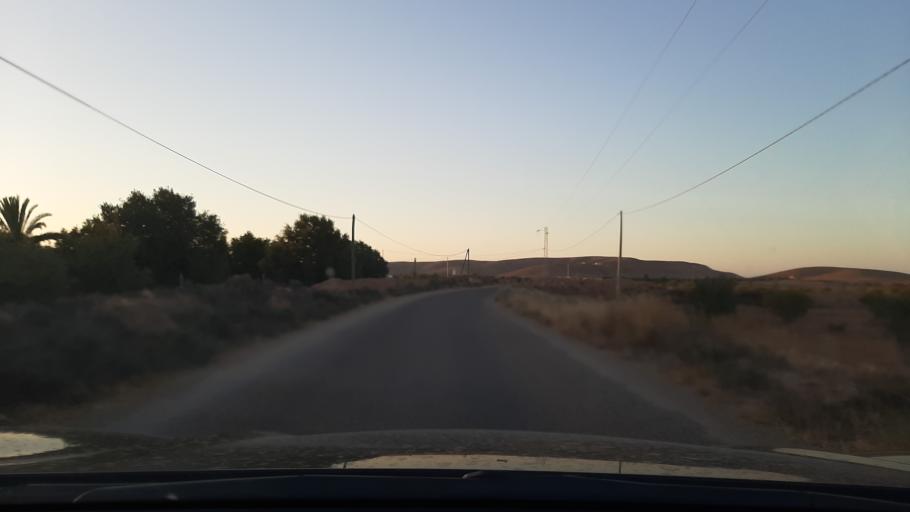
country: TN
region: Qabis
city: Matmata
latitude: 33.5601
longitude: 10.1828
